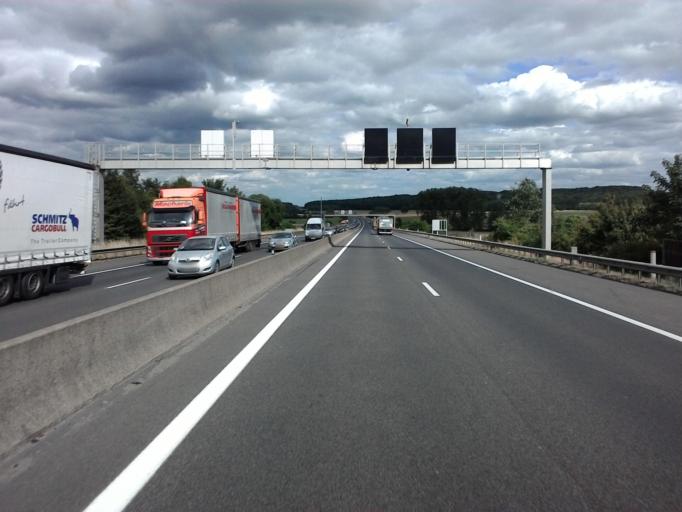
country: LU
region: Luxembourg
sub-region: Canton de Capellen
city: Steinfort
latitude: 49.6371
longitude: 5.9177
